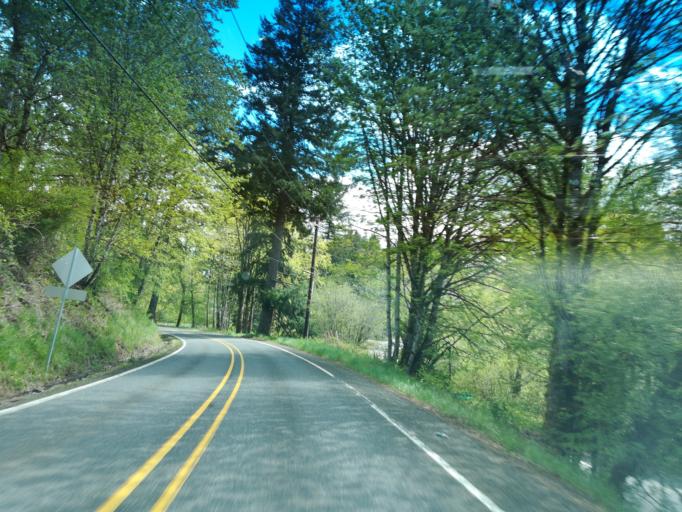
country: US
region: Oregon
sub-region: Clackamas County
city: Damascus
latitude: 45.4389
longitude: -122.4503
